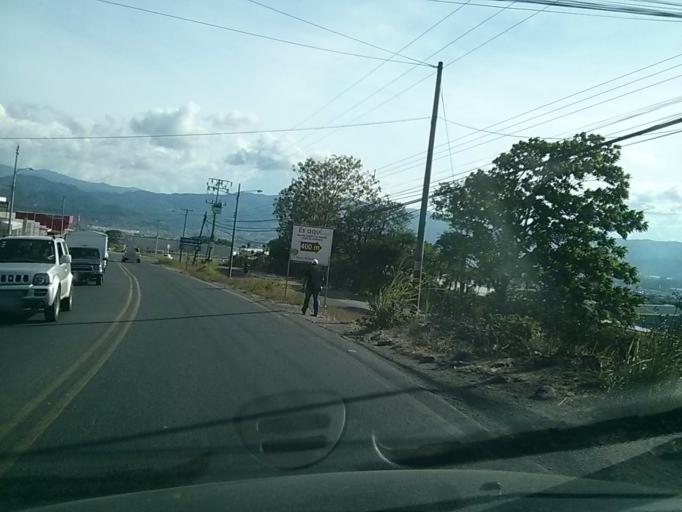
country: CR
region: Cartago
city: Cartago
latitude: 9.8810
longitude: -83.9222
